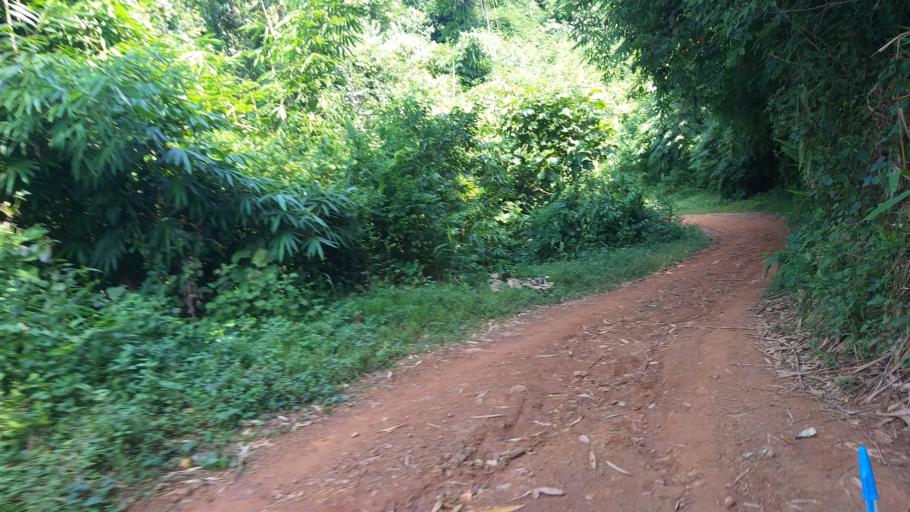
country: LA
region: Phongsali
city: Khoa
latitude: 21.3280
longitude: 102.5666
